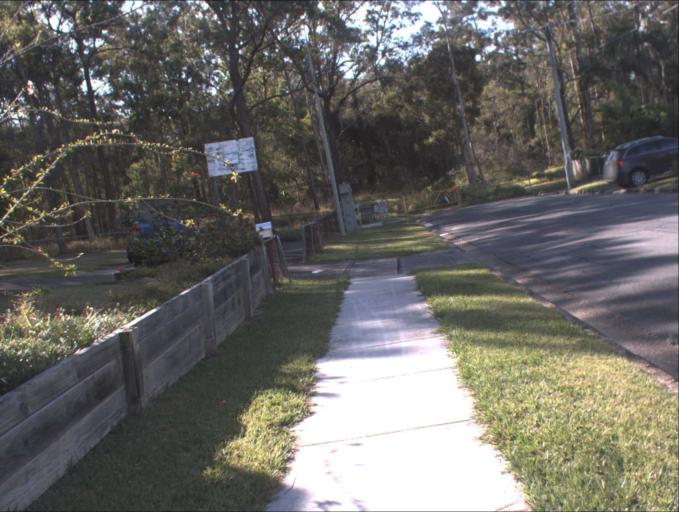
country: AU
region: Queensland
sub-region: Logan
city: Woodridge
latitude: -27.6246
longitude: 153.0975
